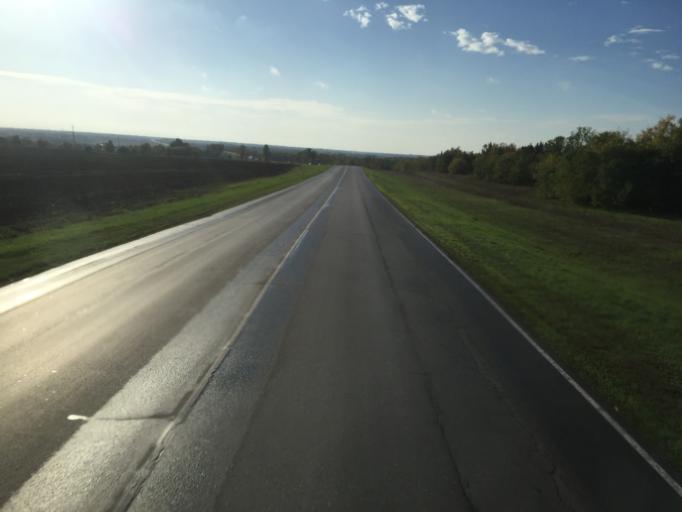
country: RU
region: Rostov
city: Mechetinskaya
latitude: 46.6776
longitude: 40.5253
